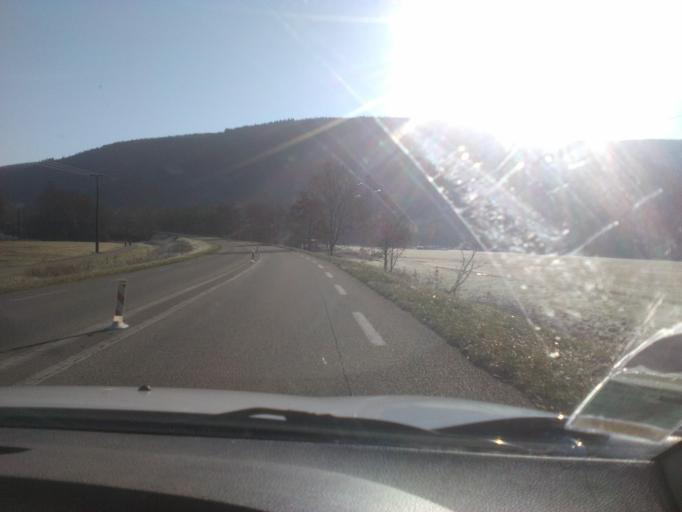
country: FR
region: Alsace
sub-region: Departement du Bas-Rhin
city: Niederhaslach
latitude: 48.5205
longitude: 7.3586
